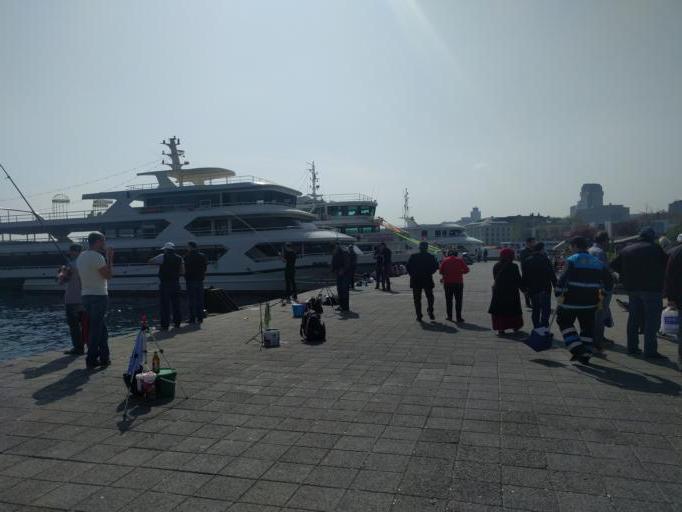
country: TR
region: Istanbul
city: UEskuedar
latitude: 41.0414
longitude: 29.0099
